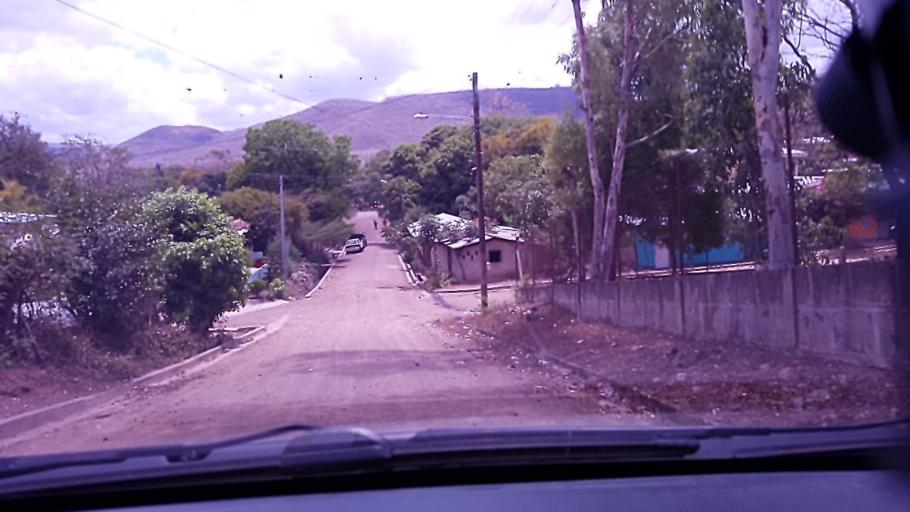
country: NI
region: Esteli
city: Condega
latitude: 13.3678
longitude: -86.3976
